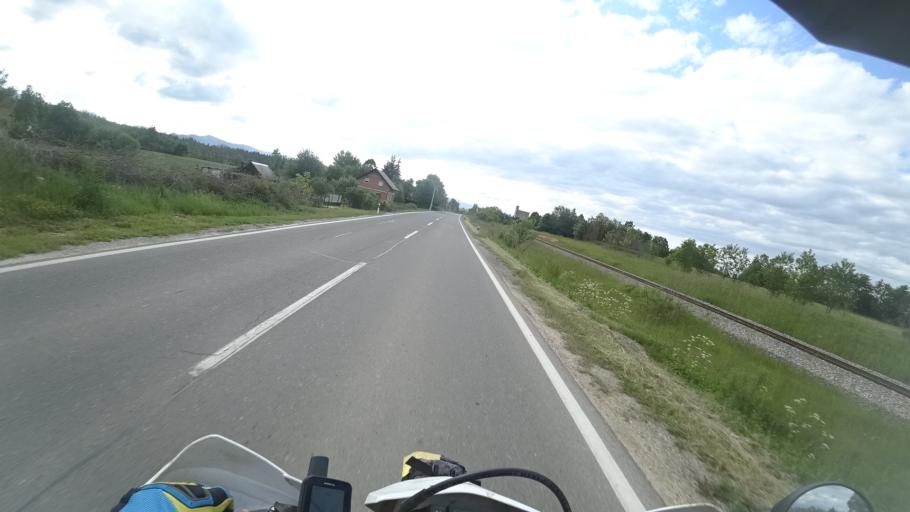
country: HR
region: Licko-Senjska
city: Gospic
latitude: 44.5283
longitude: 15.4064
